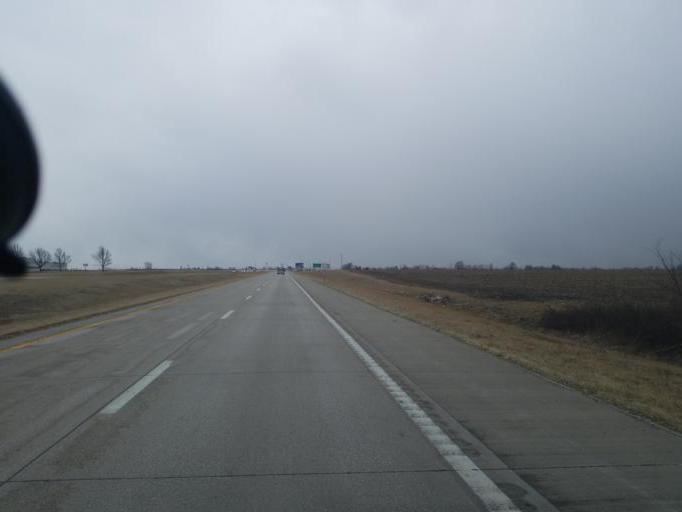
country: US
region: Missouri
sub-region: Randolph County
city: Moberly
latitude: 39.4670
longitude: -92.4351
